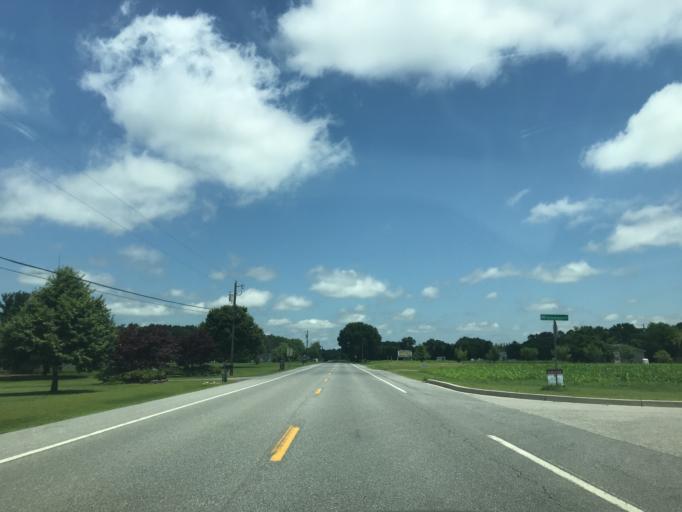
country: US
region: Maryland
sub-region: Caroline County
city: Federalsburg
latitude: 38.7043
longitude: -75.7531
